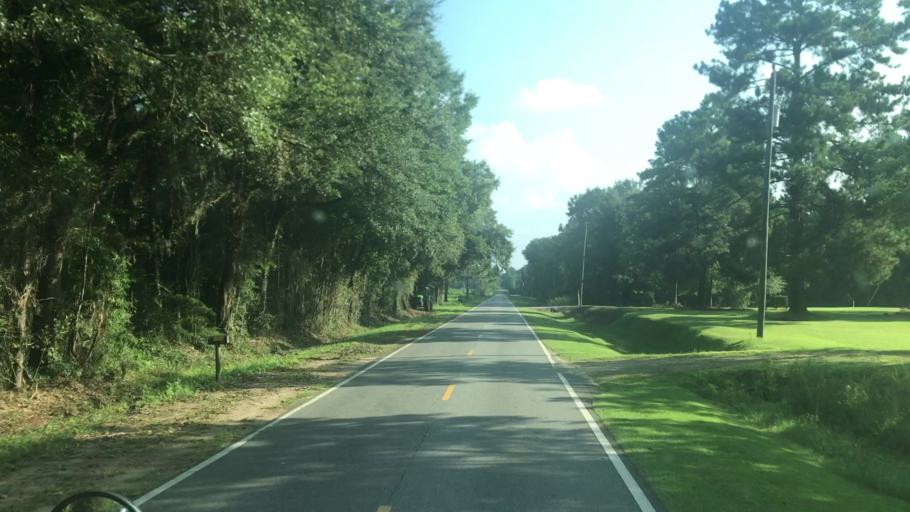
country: US
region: Florida
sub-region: Gadsden County
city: Quincy
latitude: 30.6818
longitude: -84.5402
